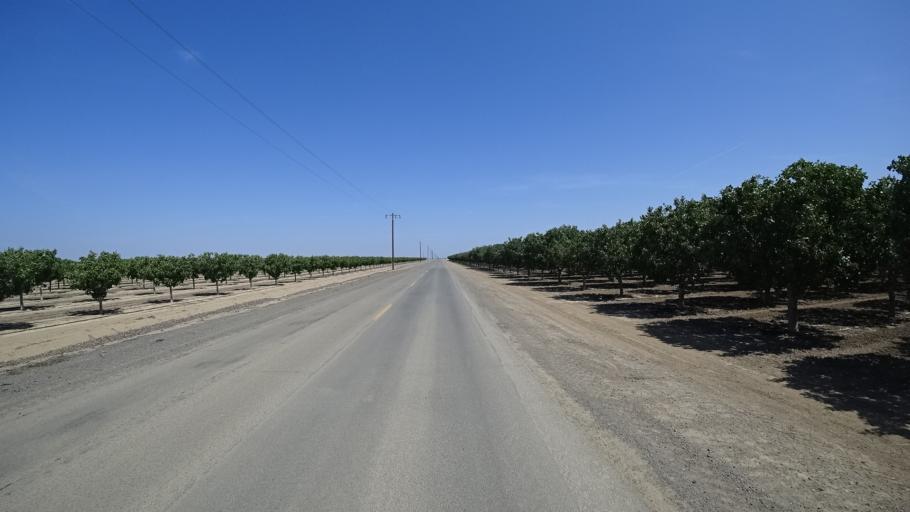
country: US
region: California
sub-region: Kings County
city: Kettleman City
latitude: 36.1044
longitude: -120.0037
